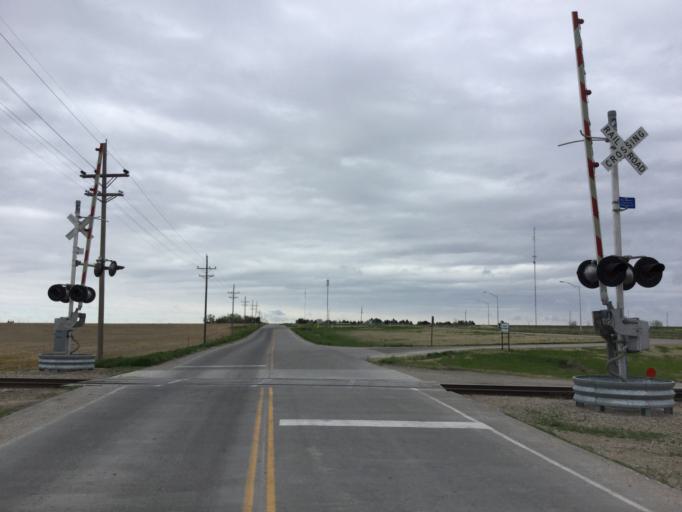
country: US
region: Kansas
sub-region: Phillips County
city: Phillipsburg
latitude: 39.7595
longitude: -99.3093
